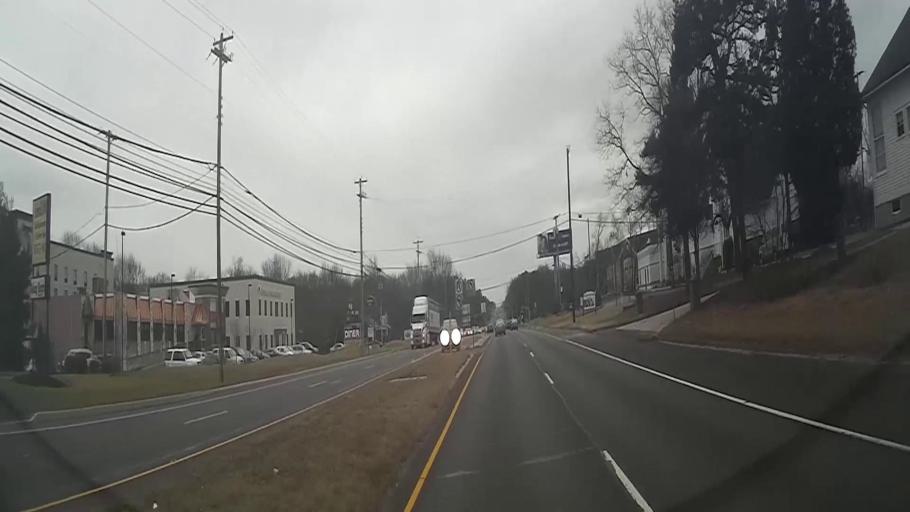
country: US
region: New Jersey
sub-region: Burlington County
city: Marlton
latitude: 39.8515
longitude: -74.9223
